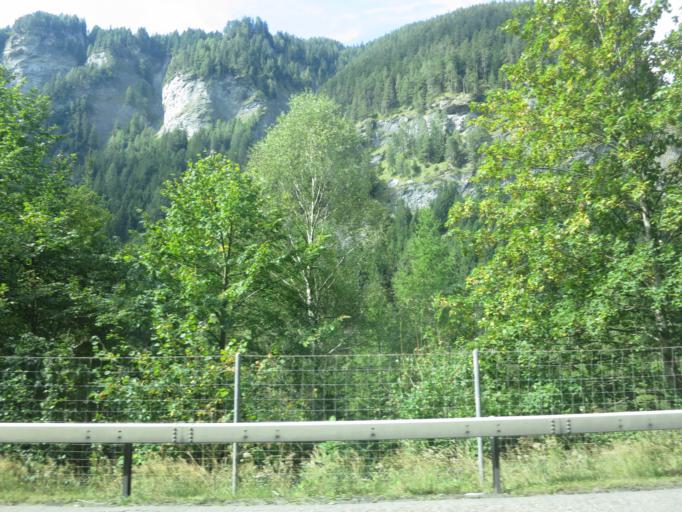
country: CH
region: Grisons
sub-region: Hinterrhein District
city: Thusis
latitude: 46.6526
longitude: 9.4512
